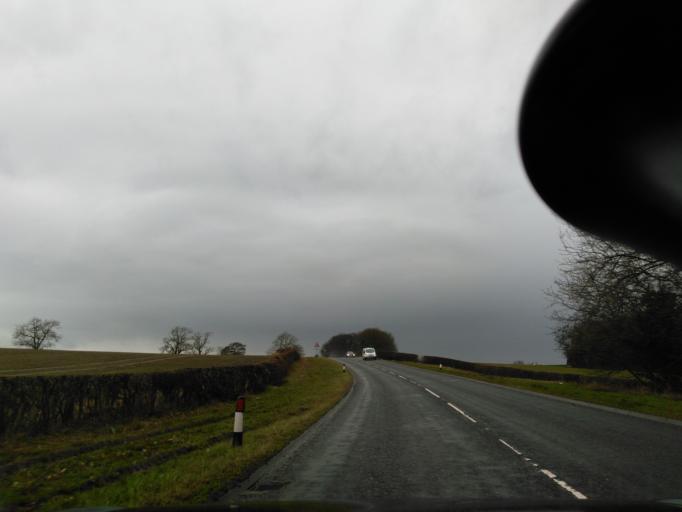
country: GB
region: England
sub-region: North Yorkshire
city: Thirsk
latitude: 54.2843
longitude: -1.3801
